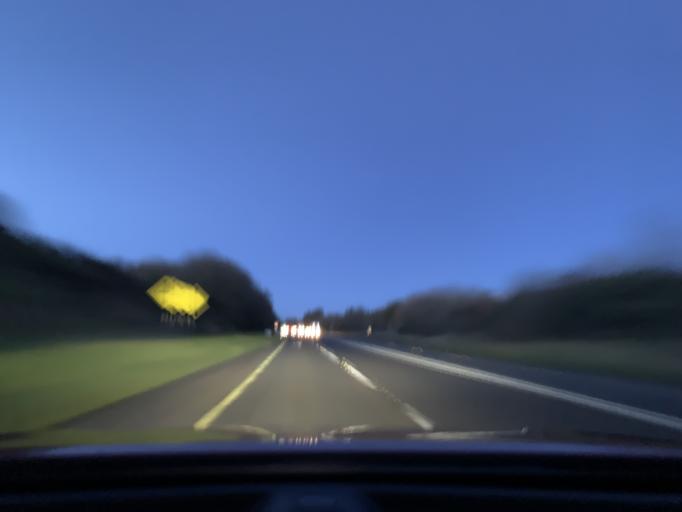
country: IE
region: Connaught
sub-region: Roscommon
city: Boyle
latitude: 53.9929
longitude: -8.2797
